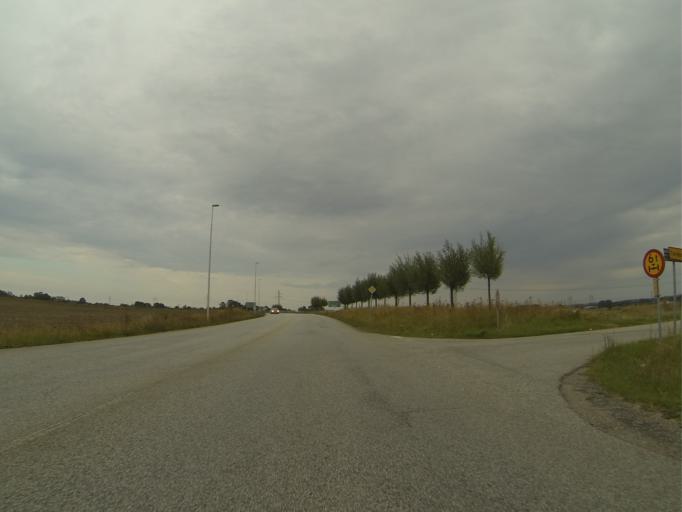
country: SE
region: Skane
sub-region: Burlovs Kommun
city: Arloev
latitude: 55.6312
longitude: 13.1057
